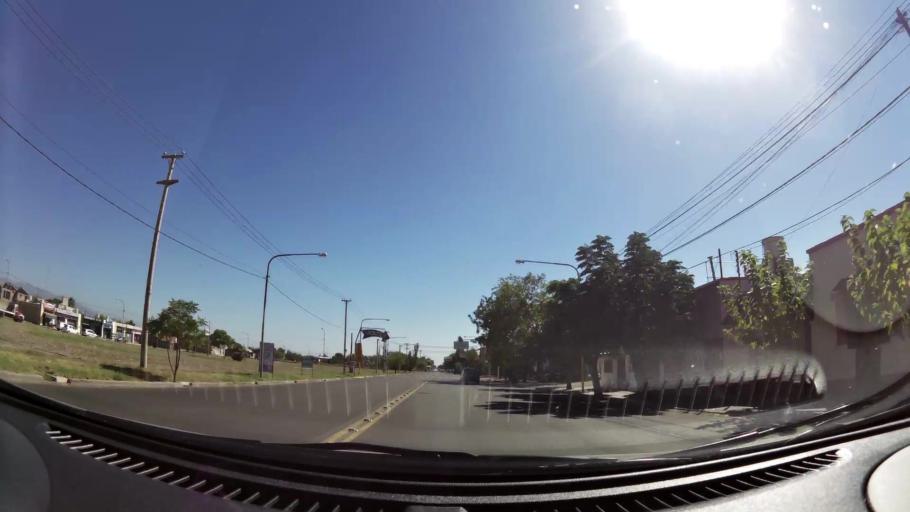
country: AR
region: Mendoza
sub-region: Departamento de Maipu
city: Maipu
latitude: -32.9675
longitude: -68.7920
